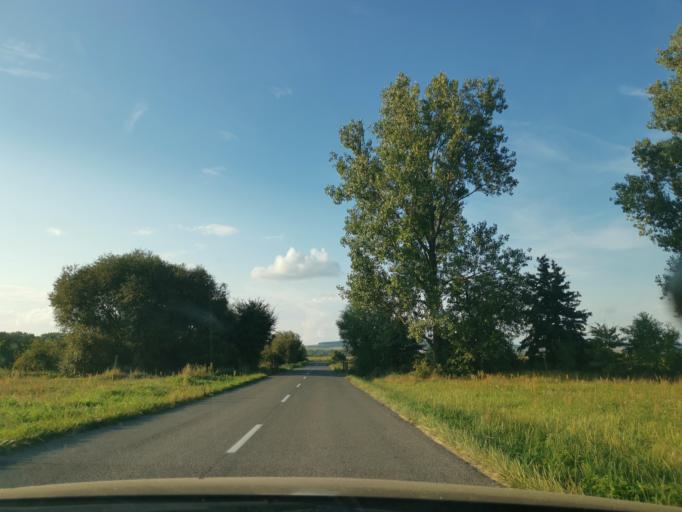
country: SK
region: Trnavsky
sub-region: Okres Senica
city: Senica
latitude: 48.6624
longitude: 17.2629
